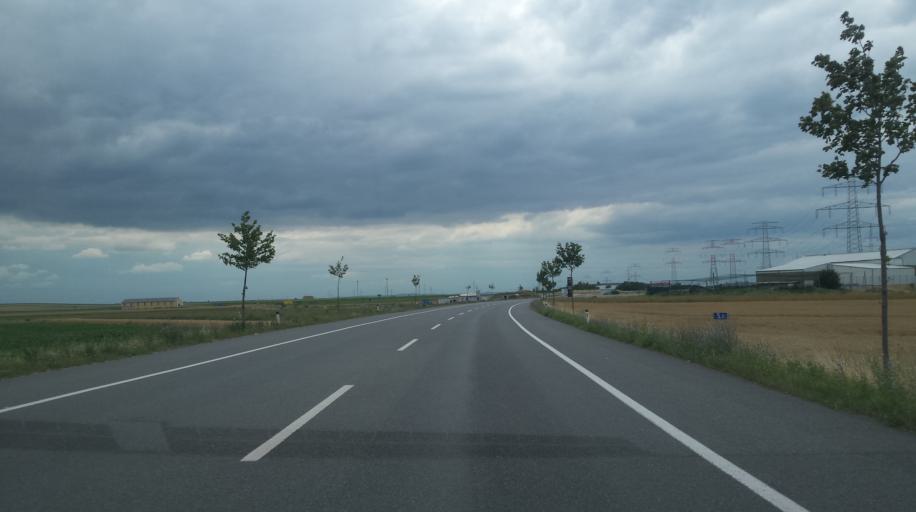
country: AT
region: Lower Austria
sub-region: Politischer Bezirk Wien-Umgebung
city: Himberg
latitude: 48.0876
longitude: 16.4550
